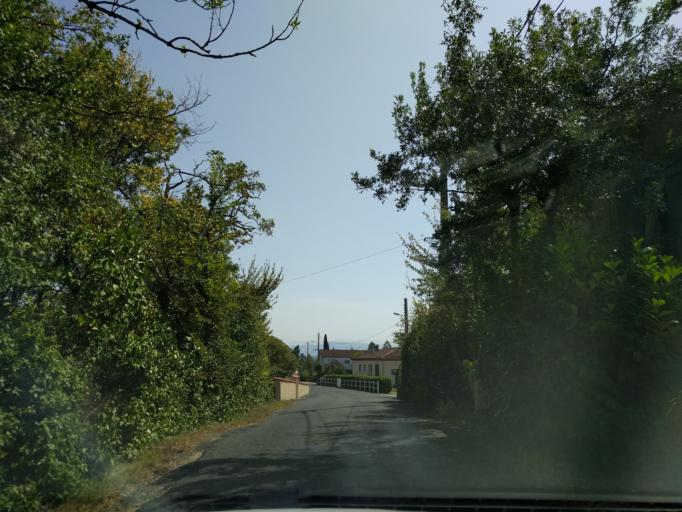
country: FR
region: Midi-Pyrenees
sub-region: Departement du Tarn
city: Castres
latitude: 43.5955
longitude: 2.2568
